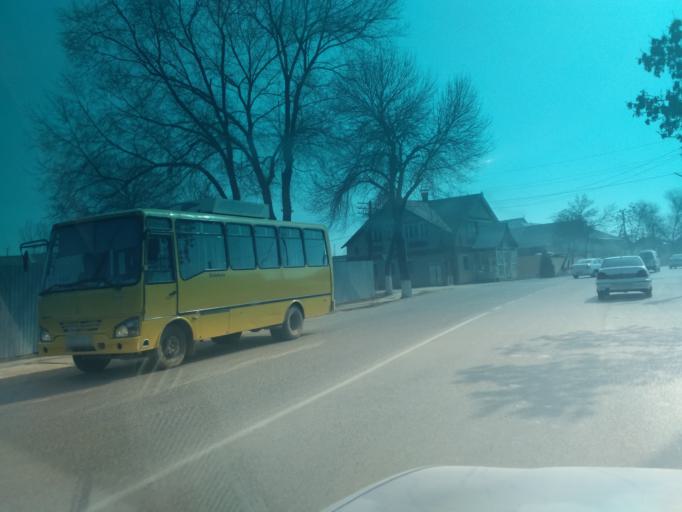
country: UZ
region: Sirdaryo
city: Guliston
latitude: 40.4892
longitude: 68.7774
